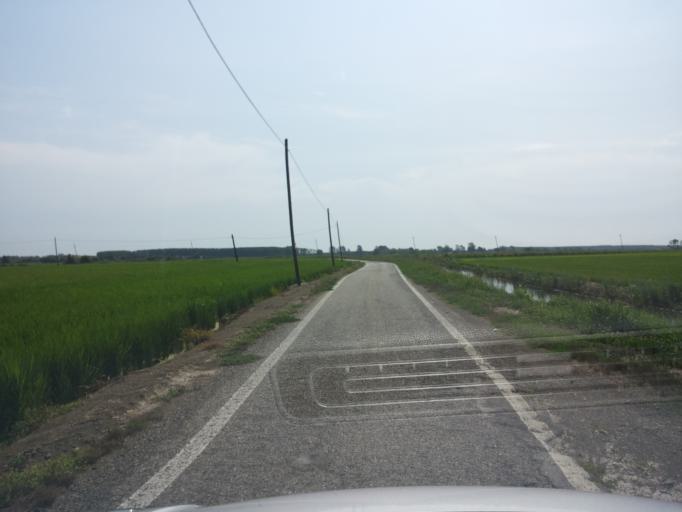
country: IT
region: Piedmont
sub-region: Provincia di Vercelli
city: Pezzana
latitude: 45.2654
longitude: 8.5174
